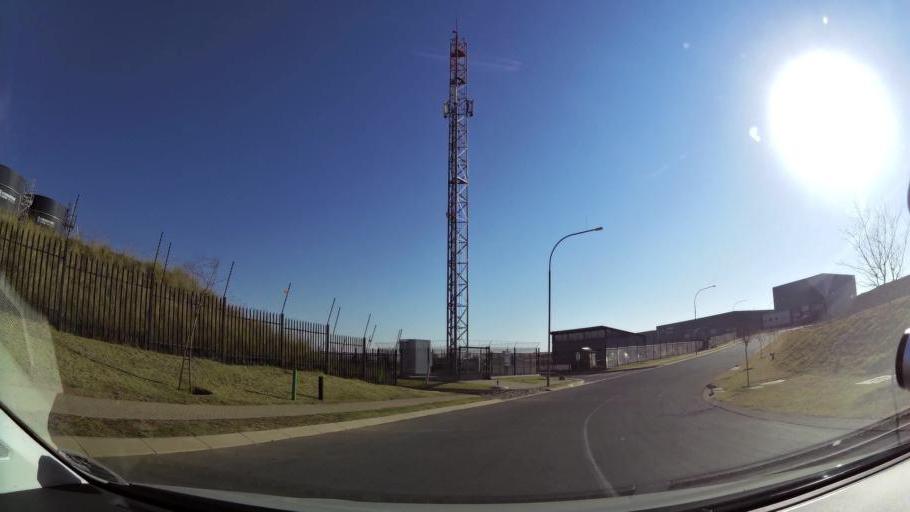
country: ZA
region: Gauteng
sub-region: City of Johannesburg Metropolitan Municipality
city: Modderfontein
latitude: -26.0513
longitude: 28.1675
